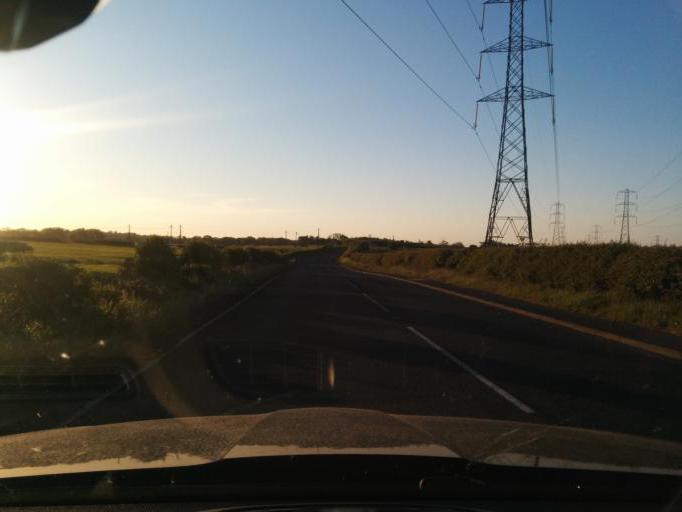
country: GB
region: England
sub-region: Northumberland
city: Bedlington
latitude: 55.1156
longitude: -1.5737
